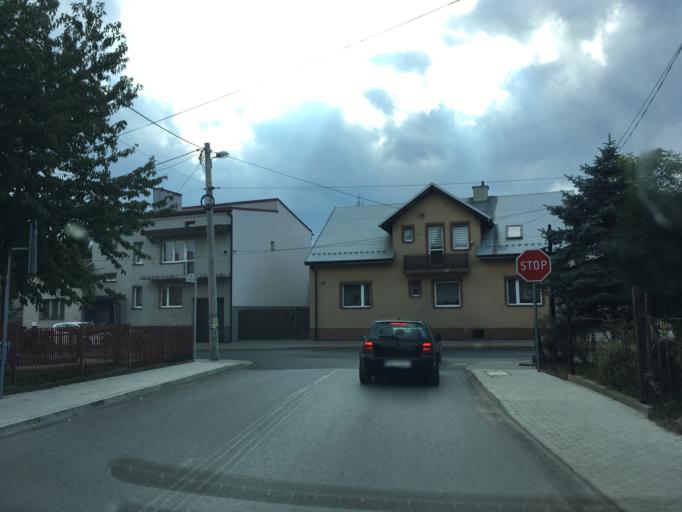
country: PL
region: Lesser Poland Voivodeship
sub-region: Powiat krakowski
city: Skala
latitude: 50.2335
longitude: 19.8509
